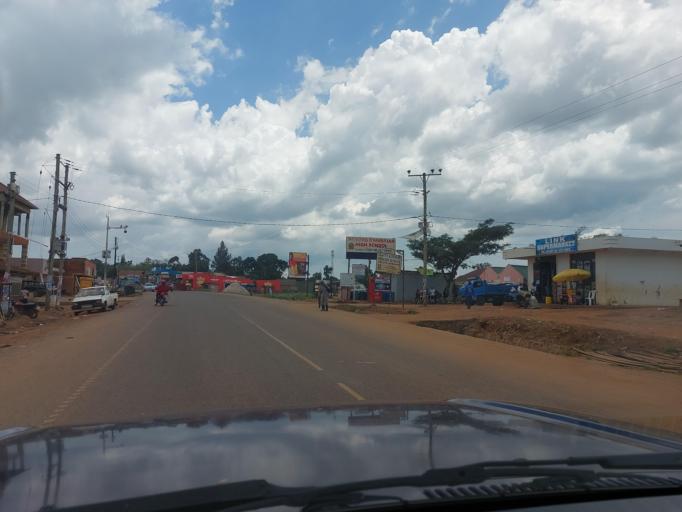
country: UG
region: Central Region
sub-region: Mukono District
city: Mukono
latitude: 0.3171
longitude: 32.7697
